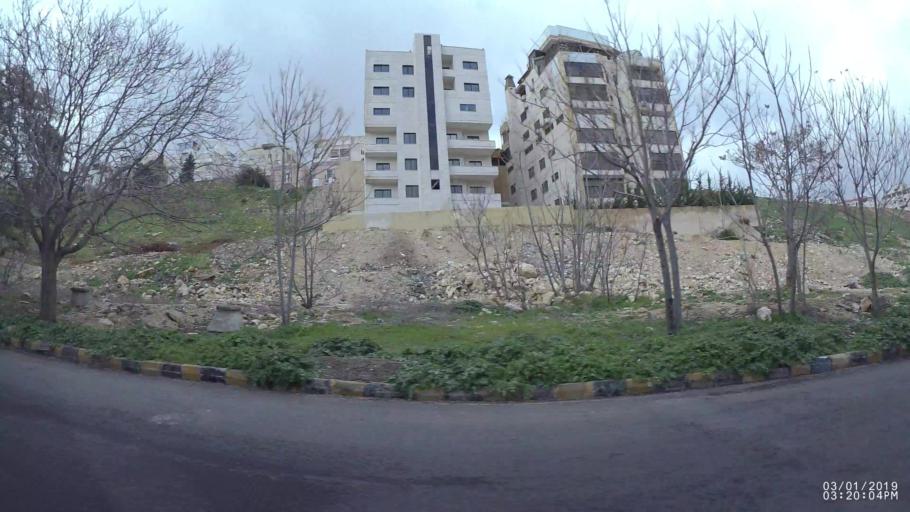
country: JO
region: Amman
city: Al Bunayyat ash Shamaliyah
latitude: 31.9422
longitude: 35.8960
